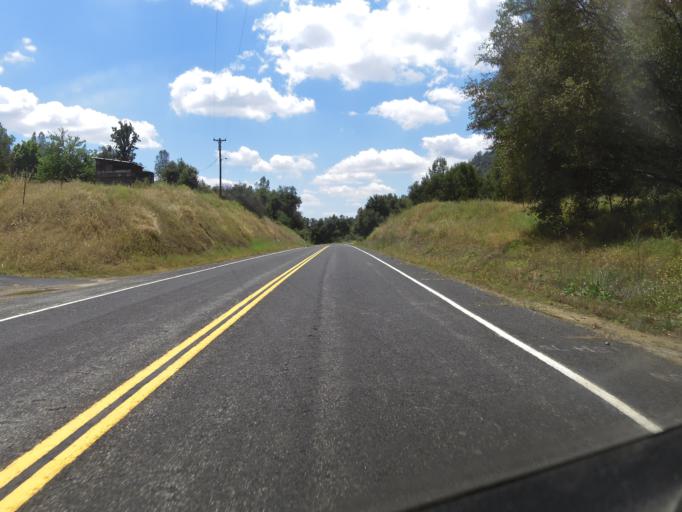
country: US
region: California
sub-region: Madera County
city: Coarsegold
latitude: 37.1879
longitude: -119.6219
